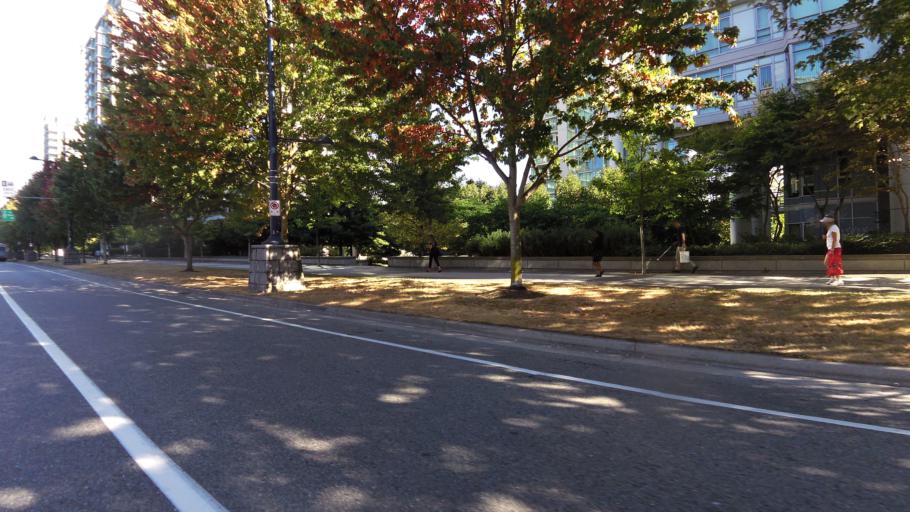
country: CA
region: British Columbia
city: West End
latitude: 49.2911
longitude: -123.1312
